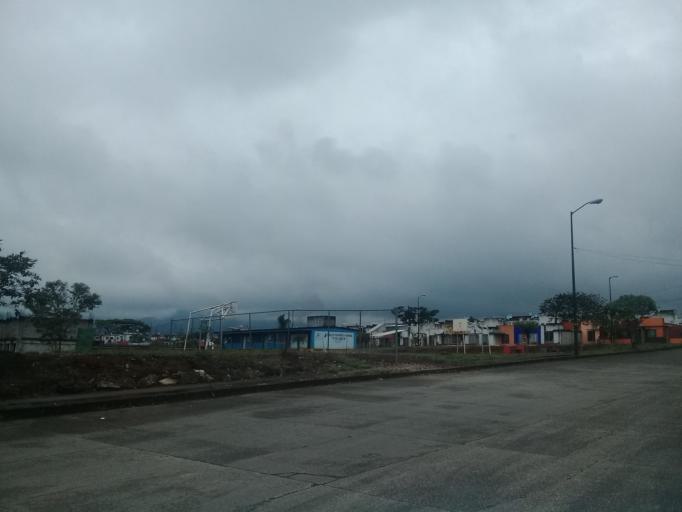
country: MX
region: Veracruz
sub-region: Amatlan de los Reyes
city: Trapiche Viejo
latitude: 18.8374
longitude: -96.9530
